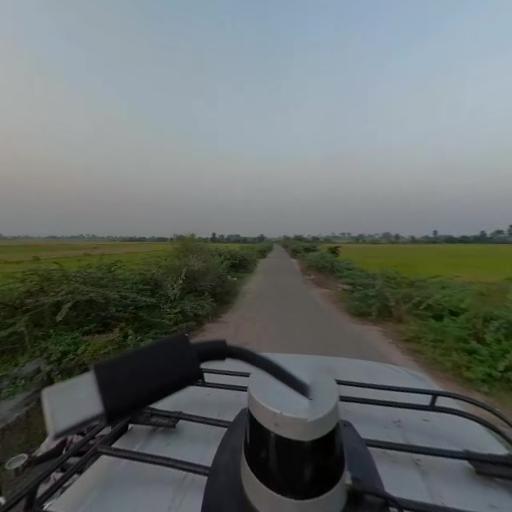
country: IN
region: Telangana
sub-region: Nalgonda
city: Suriapet
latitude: 17.1090
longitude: 79.5302
